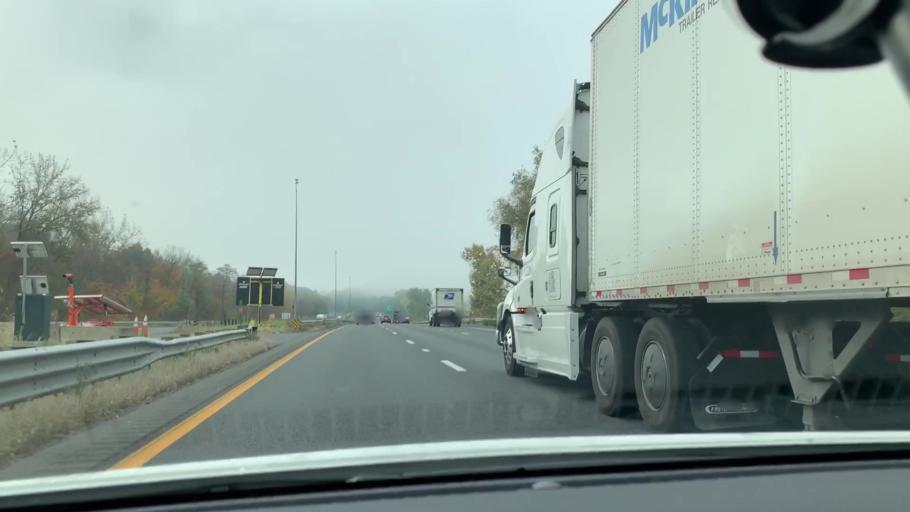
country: US
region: Massachusetts
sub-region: Hampden County
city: Longmeadow
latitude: 42.0352
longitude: -72.5891
